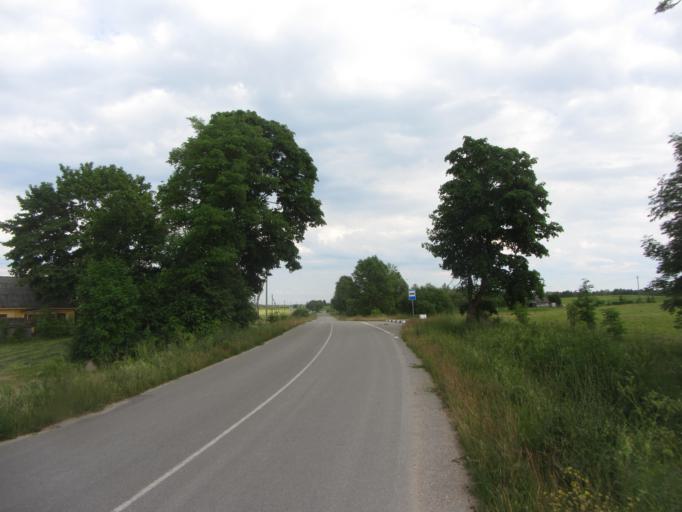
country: LT
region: Alytaus apskritis
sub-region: Alytaus rajonas
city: Daugai
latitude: 54.4669
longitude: 24.3013
